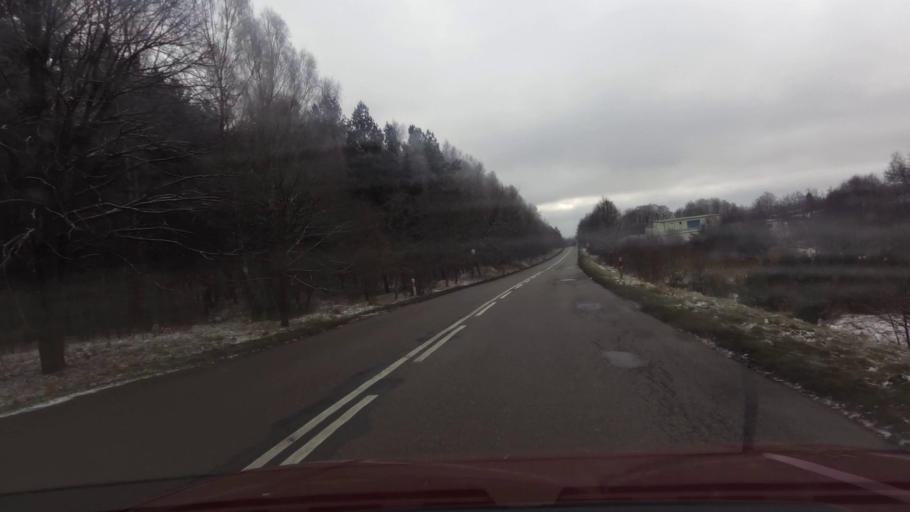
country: PL
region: West Pomeranian Voivodeship
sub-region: Powiat swidwinski
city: Polczyn-Zdroj
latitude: 53.7885
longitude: 16.0723
